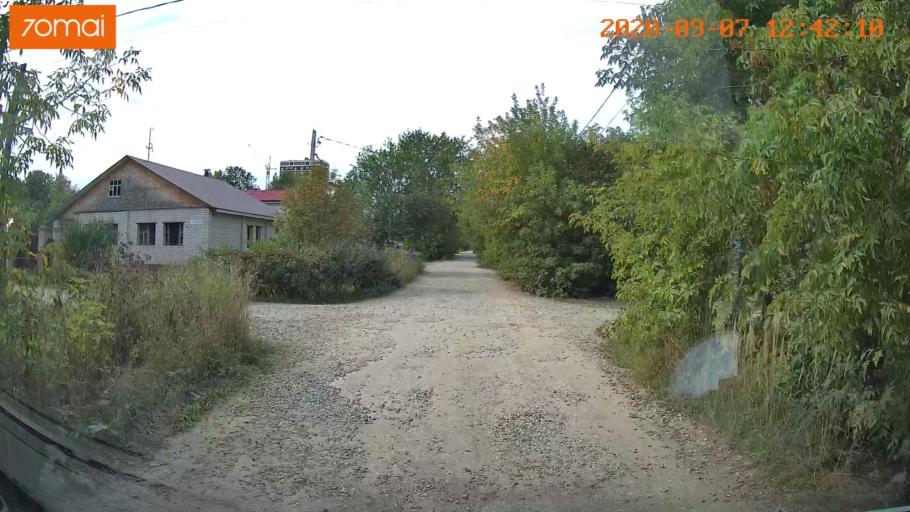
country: RU
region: Ivanovo
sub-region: Gorod Ivanovo
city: Ivanovo
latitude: 56.9737
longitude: 40.9863
